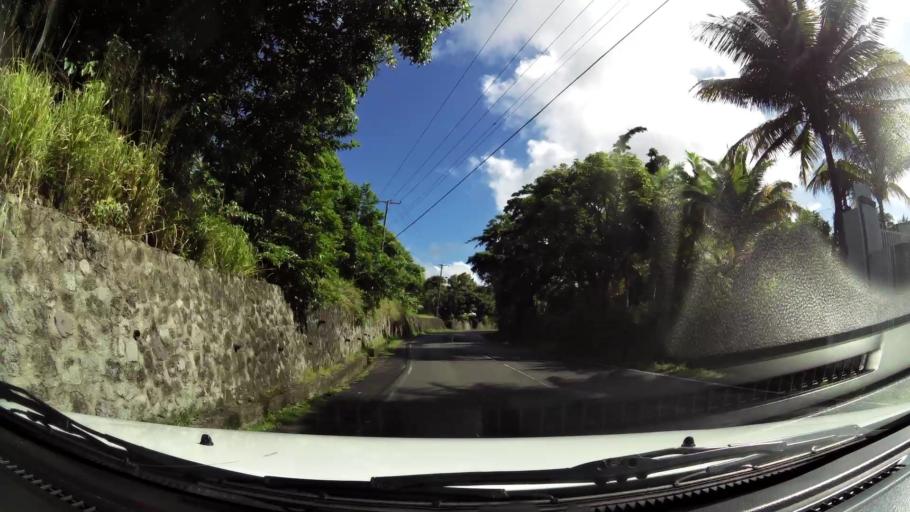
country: LC
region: Choiseul Quarter
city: Choiseul
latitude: 13.7754
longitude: -61.0343
